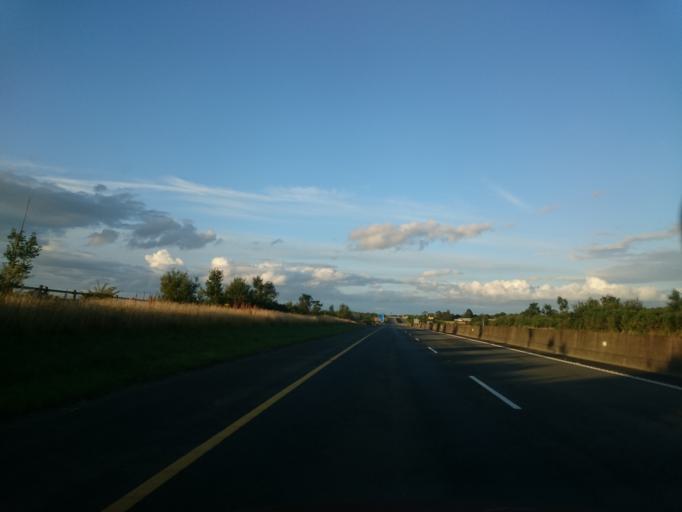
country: IE
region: Leinster
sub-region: Loch Garman
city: Gorey
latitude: 52.6582
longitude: -6.2929
